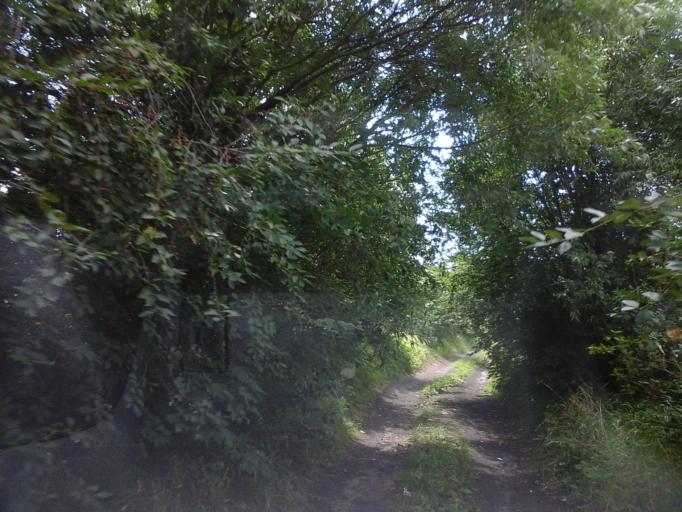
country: PL
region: West Pomeranian Voivodeship
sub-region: Powiat choszczenski
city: Recz
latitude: 53.2691
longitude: 15.4962
